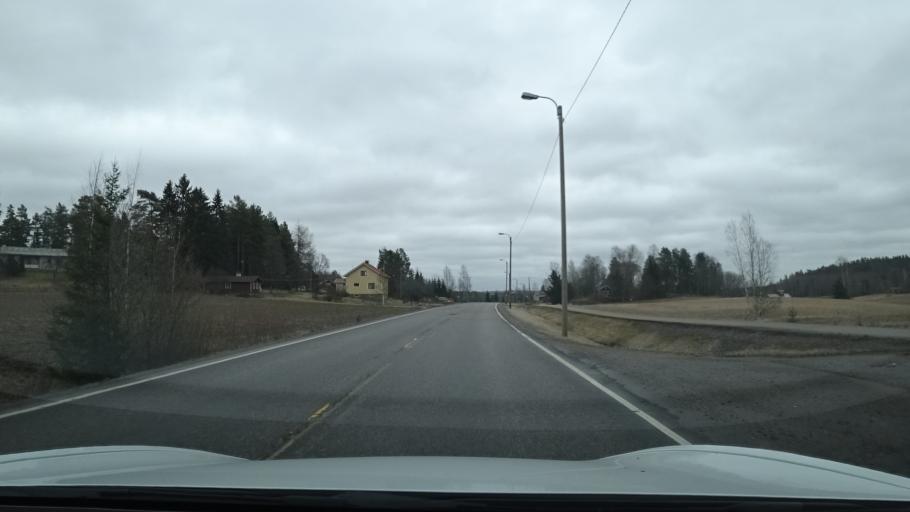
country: FI
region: Uusimaa
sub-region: Porvoo
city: Askola
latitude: 60.4959
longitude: 25.5089
